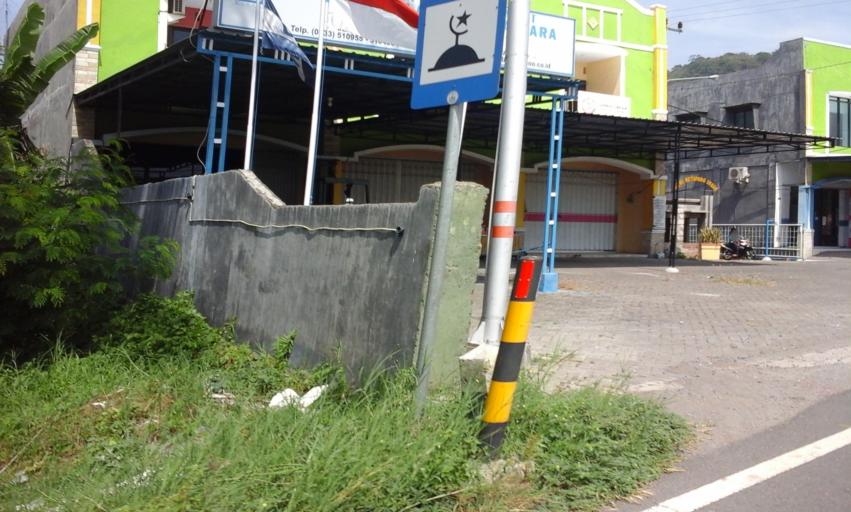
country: ID
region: East Java
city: Klatakan
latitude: -8.1248
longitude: 114.3969
